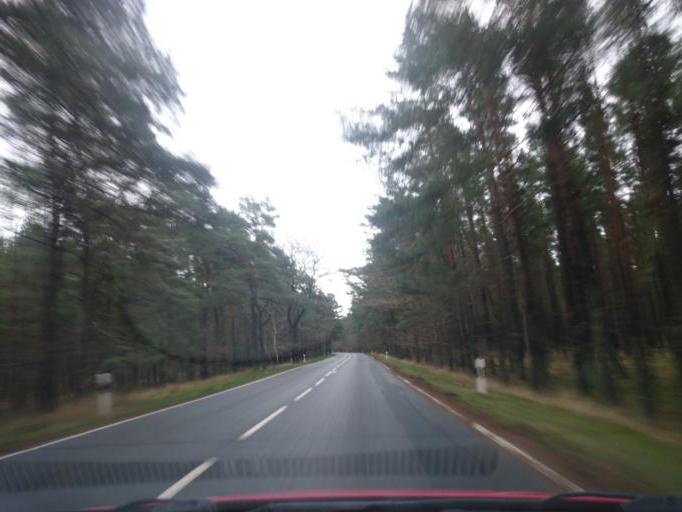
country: DE
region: Mecklenburg-Vorpommern
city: Glowe
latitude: 54.5766
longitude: 13.4157
